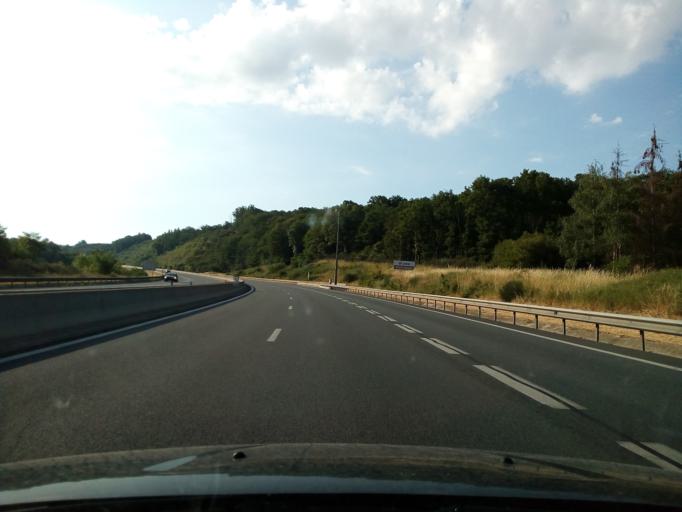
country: FR
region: Auvergne
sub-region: Departement de l'Allier
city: Desertines
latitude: 46.3700
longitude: 2.6313
